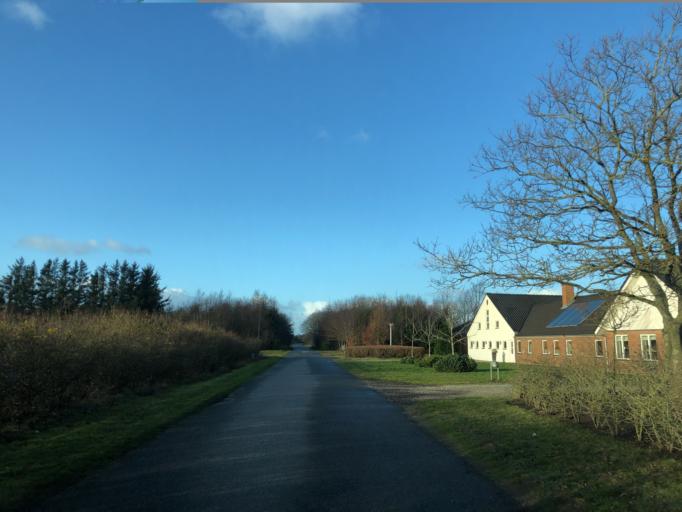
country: DK
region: Central Jutland
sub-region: Holstebro Kommune
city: Ulfborg
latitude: 56.2088
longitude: 8.2977
